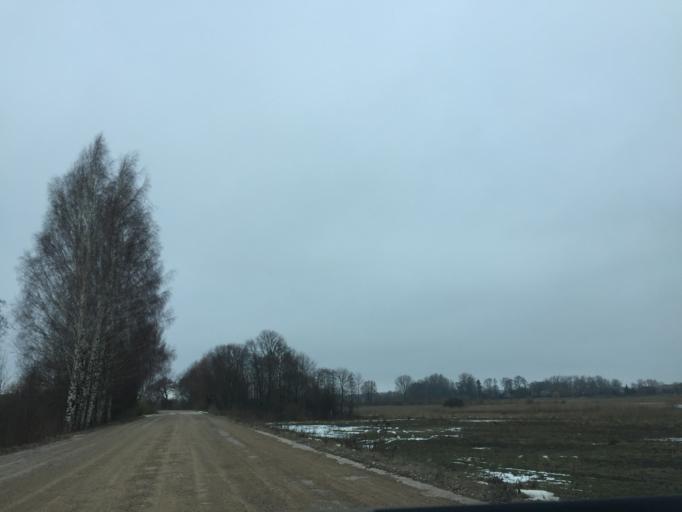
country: LV
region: Ozolnieku
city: Ozolnieki
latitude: 56.6336
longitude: 23.8029
